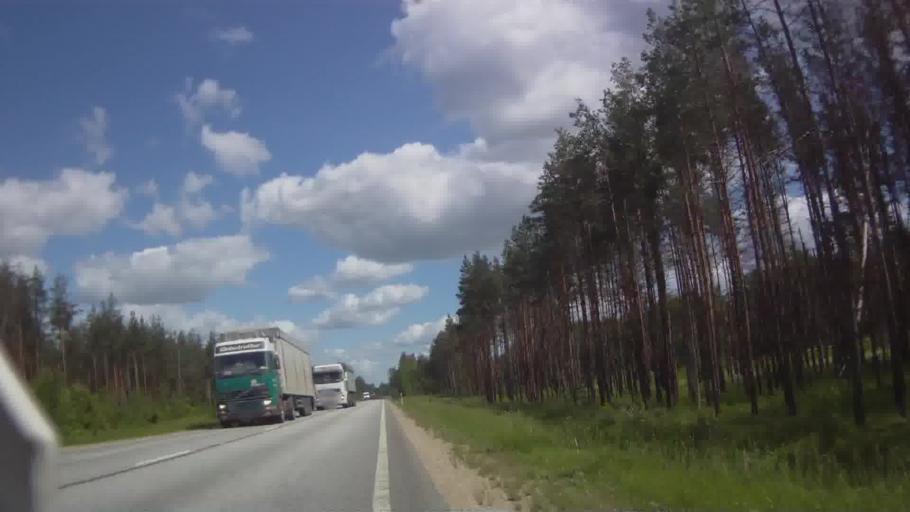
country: LV
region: Varaklani
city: Varaklani
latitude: 56.5493
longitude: 26.5903
